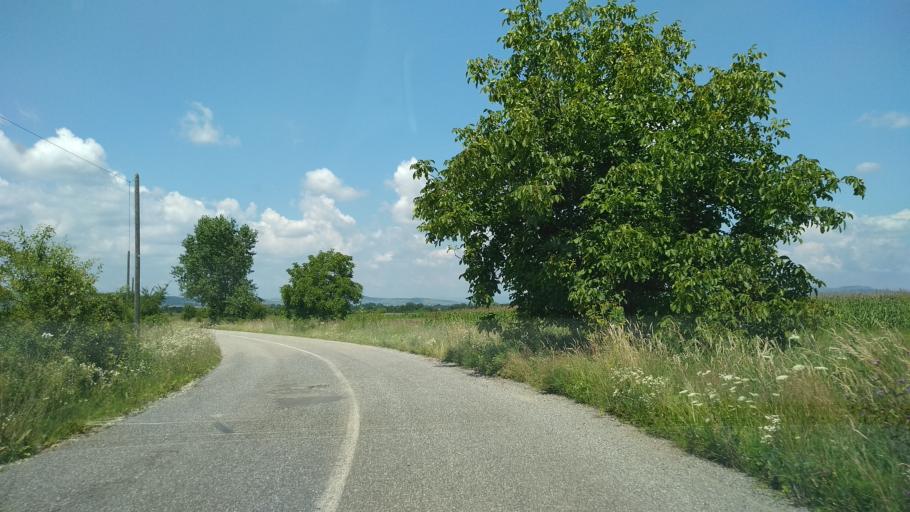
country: RO
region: Hunedoara
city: Berca
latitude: 45.6396
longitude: 23.0296
